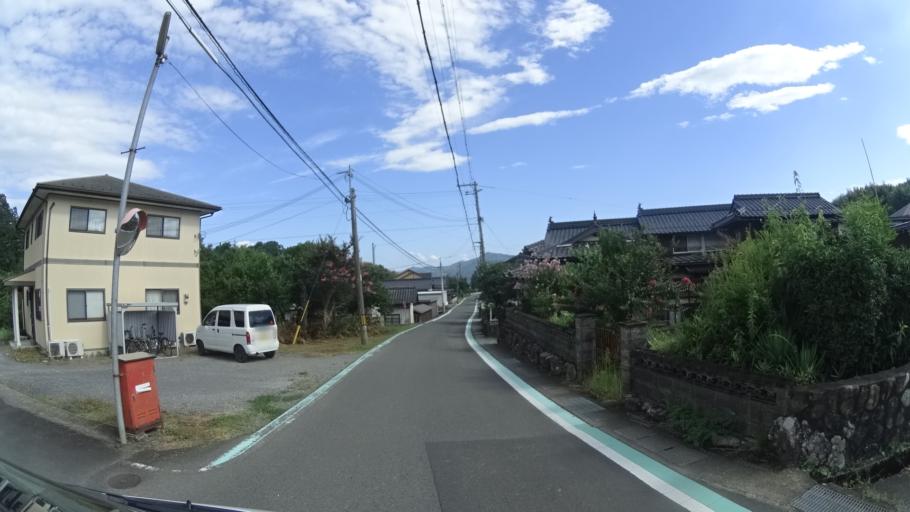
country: JP
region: Kyoto
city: Fukuchiyama
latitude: 35.3287
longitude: 135.1759
